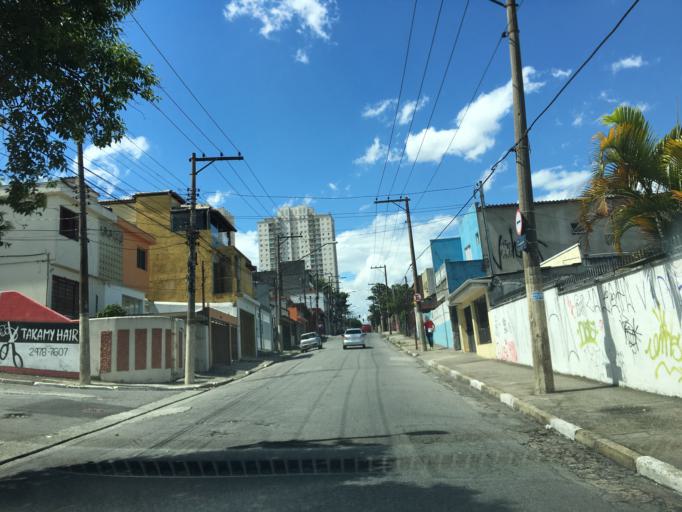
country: BR
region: Sao Paulo
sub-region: Sao Caetano Do Sul
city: Sao Caetano do Sul
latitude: -23.5808
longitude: -46.5631
